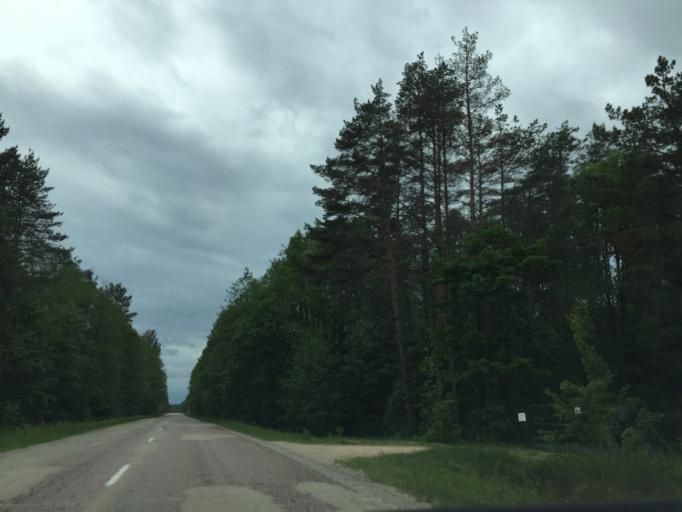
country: LV
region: Aglona
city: Aglona
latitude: 56.1477
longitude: 27.1872
